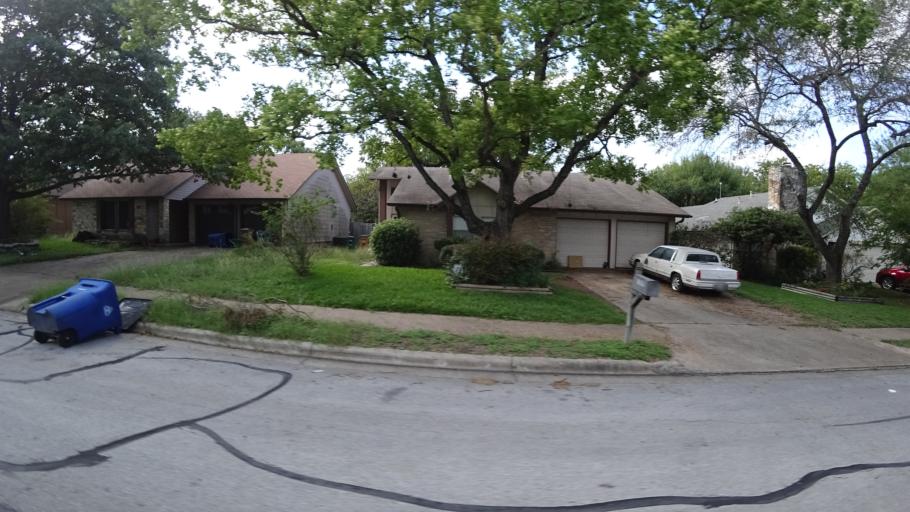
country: US
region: Texas
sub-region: Travis County
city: Rollingwood
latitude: 30.2067
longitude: -97.7948
